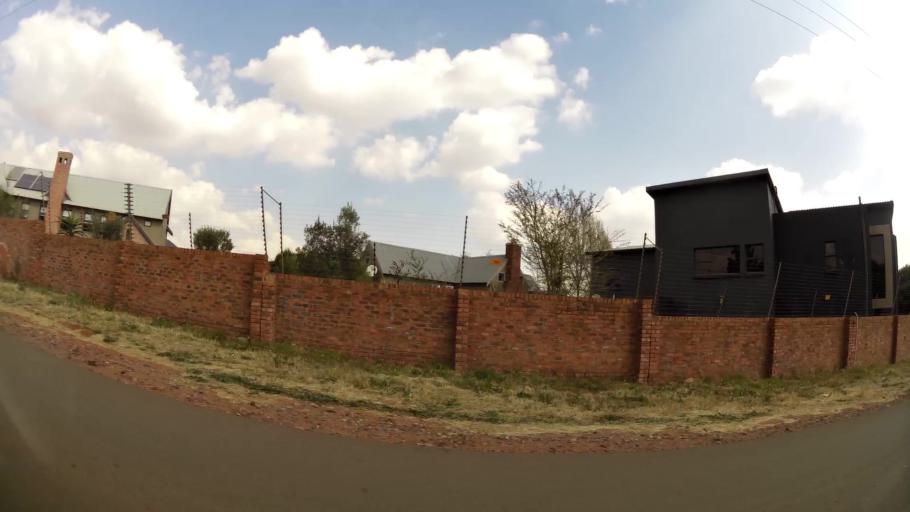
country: ZA
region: Gauteng
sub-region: City of Tshwane Metropolitan Municipality
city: Pretoria
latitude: -25.8045
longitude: 28.3471
